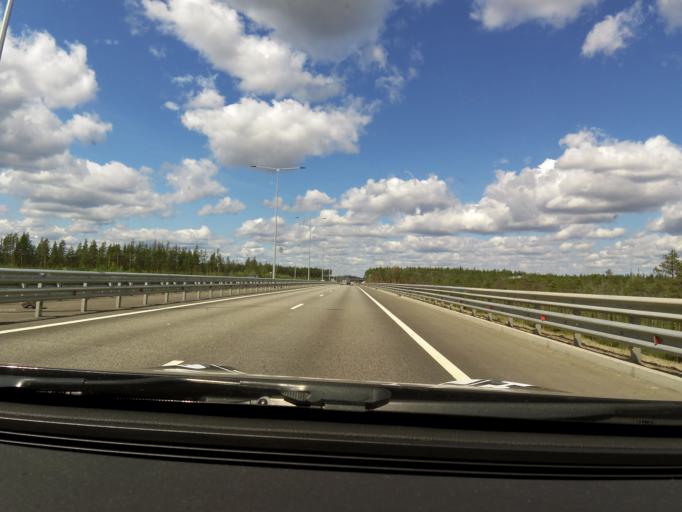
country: RU
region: Tverskaya
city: Krasnomayskiy
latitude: 57.4667
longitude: 34.3658
